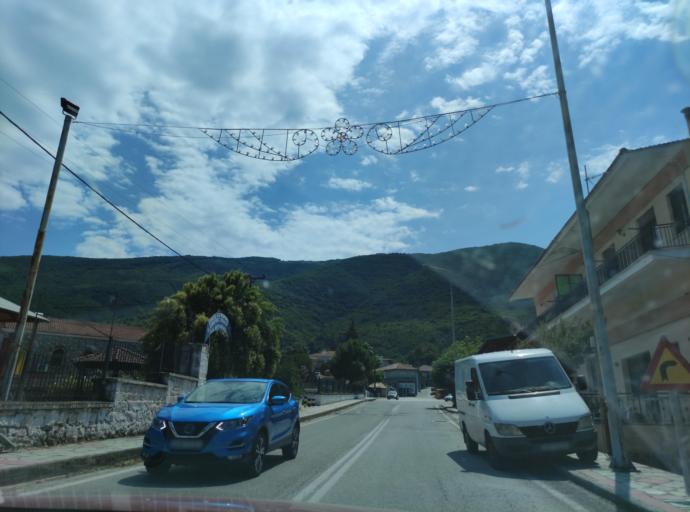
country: GR
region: East Macedonia and Thrace
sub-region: Nomos Kavalas
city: Palaiochori
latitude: 40.9472
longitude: 24.2111
